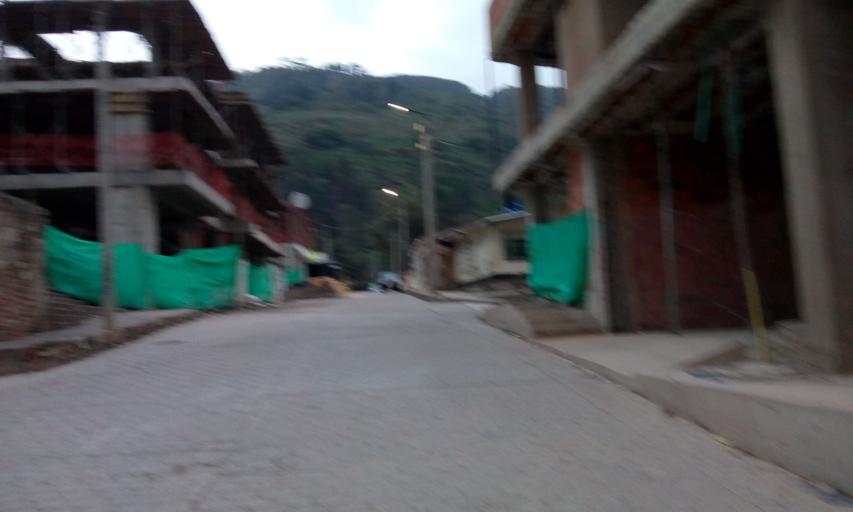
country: CO
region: Boyaca
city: Tipacoque
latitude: 6.4215
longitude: -72.6914
